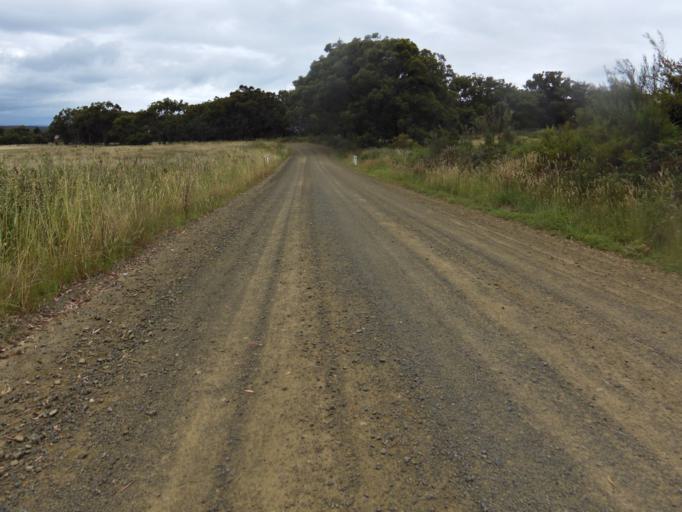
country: AU
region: Victoria
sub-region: Bass Coast
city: Cowes
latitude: -38.3827
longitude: 145.3750
